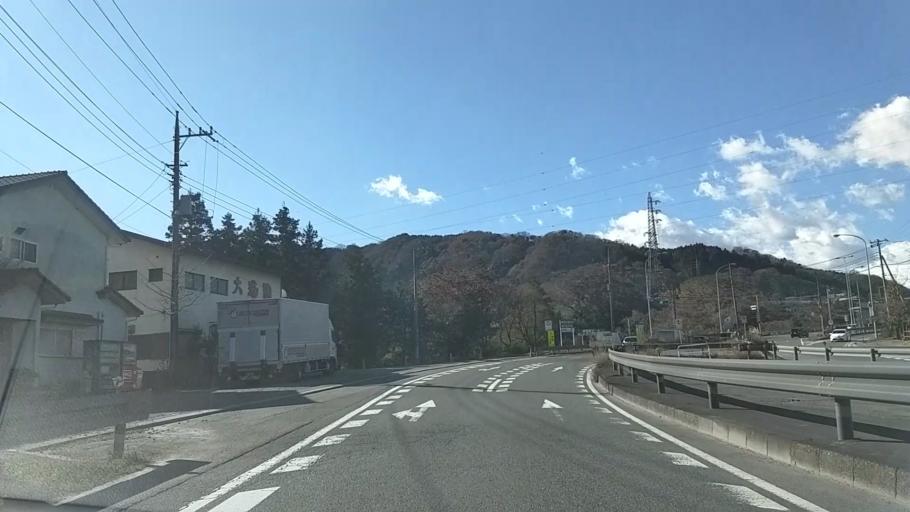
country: JP
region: Shizuoka
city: Gotemba
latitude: 35.3580
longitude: 139.0089
